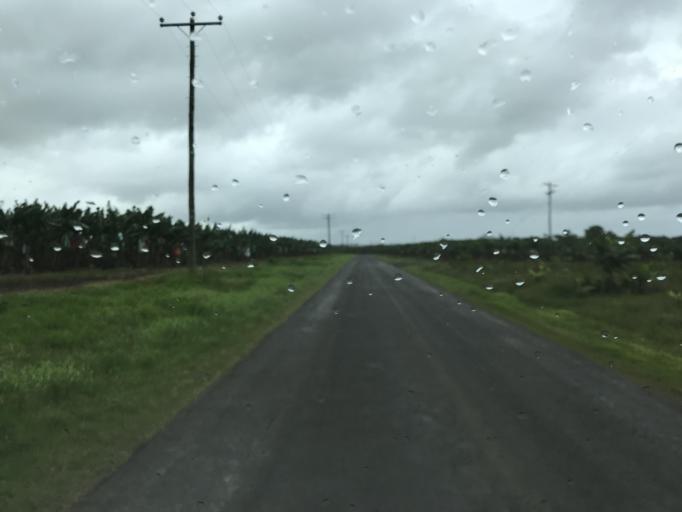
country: AU
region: Queensland
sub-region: Cassowary Coast
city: Innisfail
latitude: -17.5071
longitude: 145.9794
